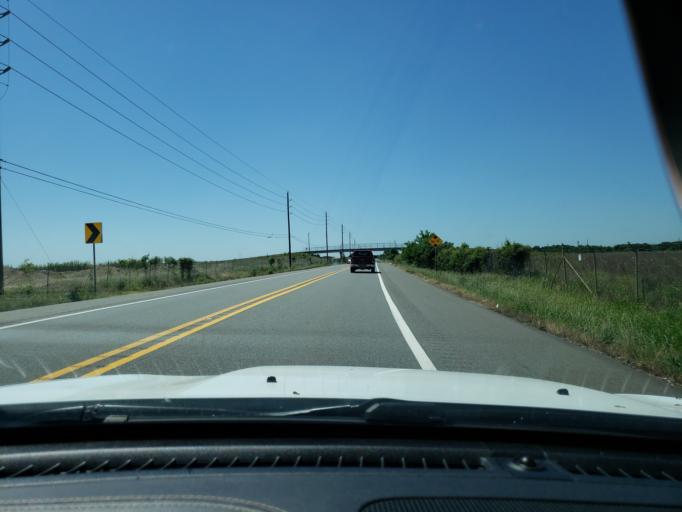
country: US
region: Texas
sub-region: Fort Bend County
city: Fulshear
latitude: 29.6840
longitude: -95.8391
